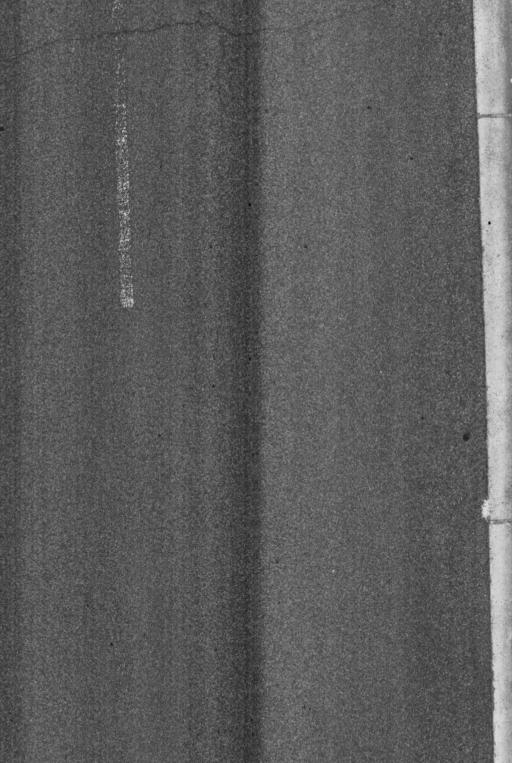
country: US
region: Washington, D.C.
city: Washington, D.C.
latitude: 38.8584
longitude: -77.0230
